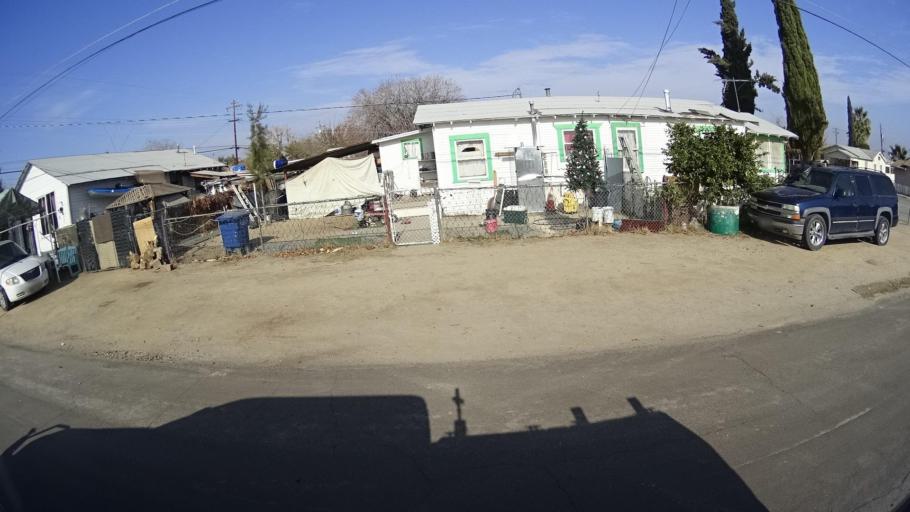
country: US
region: California
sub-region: Kern County
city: Ford City
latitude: 35.1549
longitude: -119.4603
